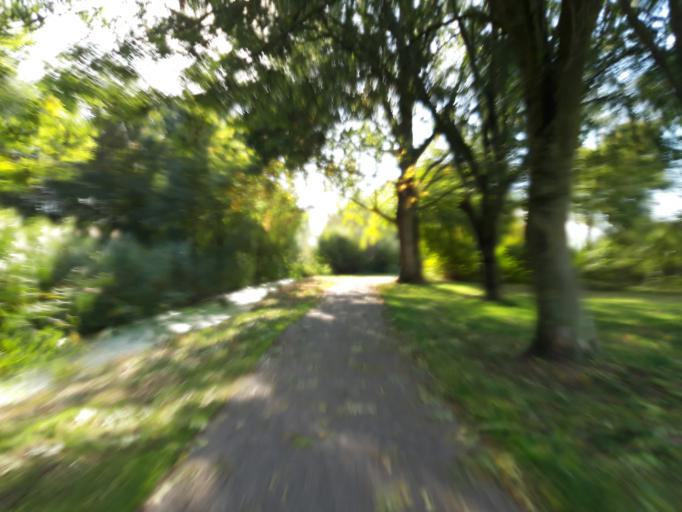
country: NL
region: Utrecht
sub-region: Gemeente Woerden
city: Woerden
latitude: 52.0748
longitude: 4.8779
